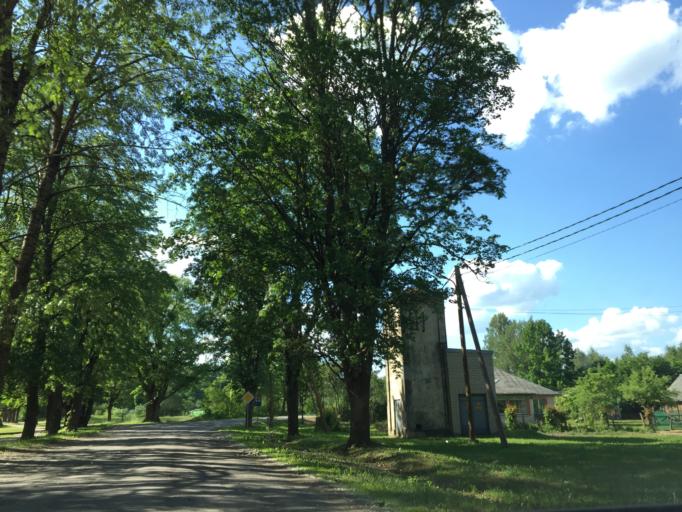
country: LV
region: Jaunpils
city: Jaunpils
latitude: 56.8761
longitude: 22.9932
